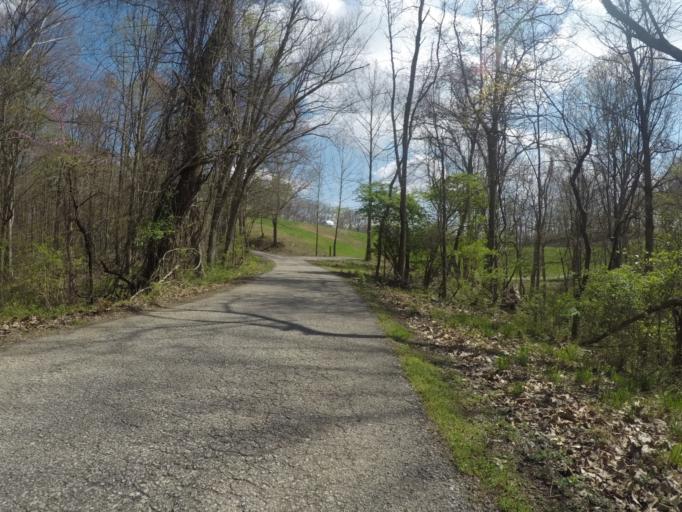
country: US
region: West Virginia
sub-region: Wayne County
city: Ceredo
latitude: 38.3879
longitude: -82.5439
